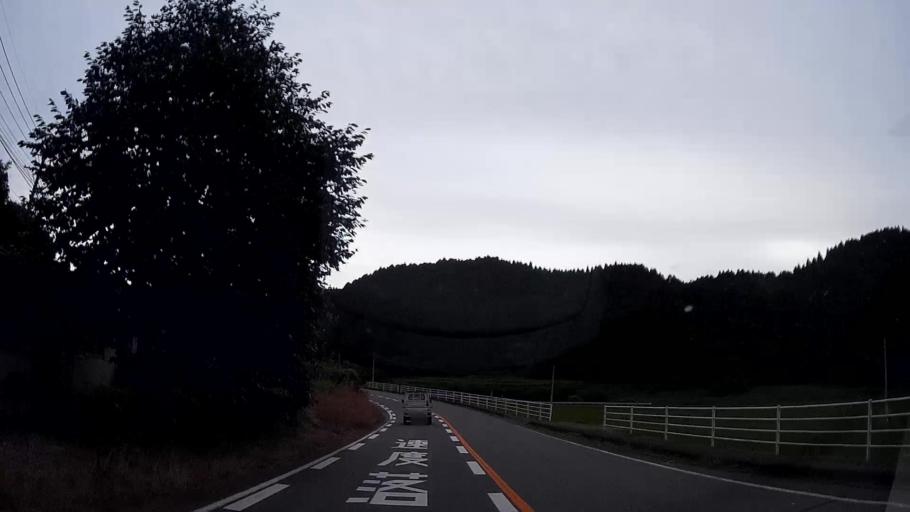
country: JP
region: Kumamoto
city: Kikuchi
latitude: 33.0157
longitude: 130.8736
